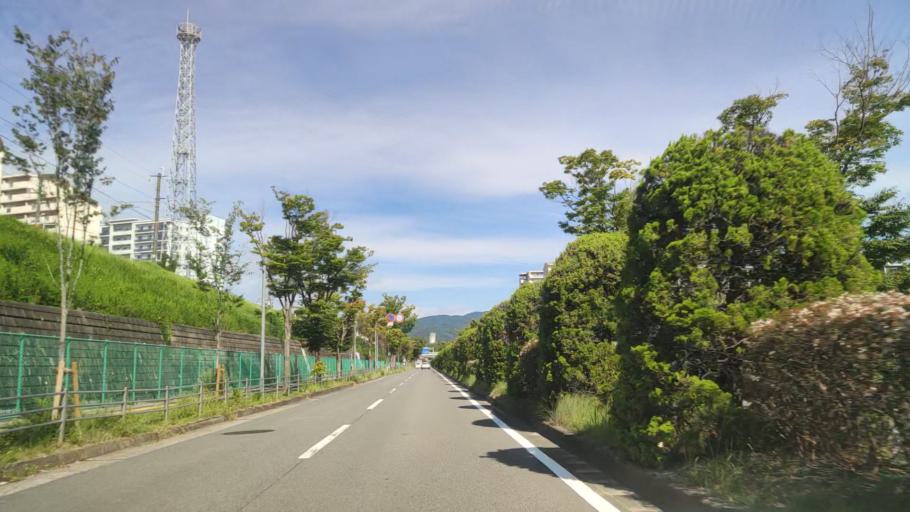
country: JP
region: Osaka
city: Mino
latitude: 34.8174
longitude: 135.5127
